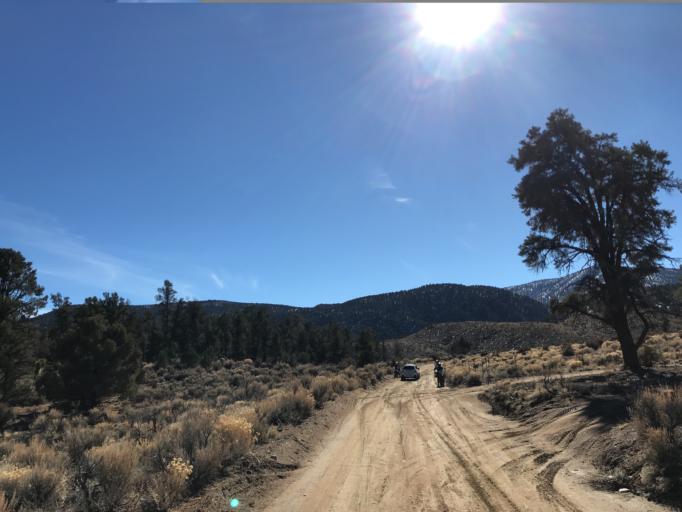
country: US
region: California
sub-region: San Bernardino County
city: Big Bear City
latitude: 34.2569
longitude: -116.7486
